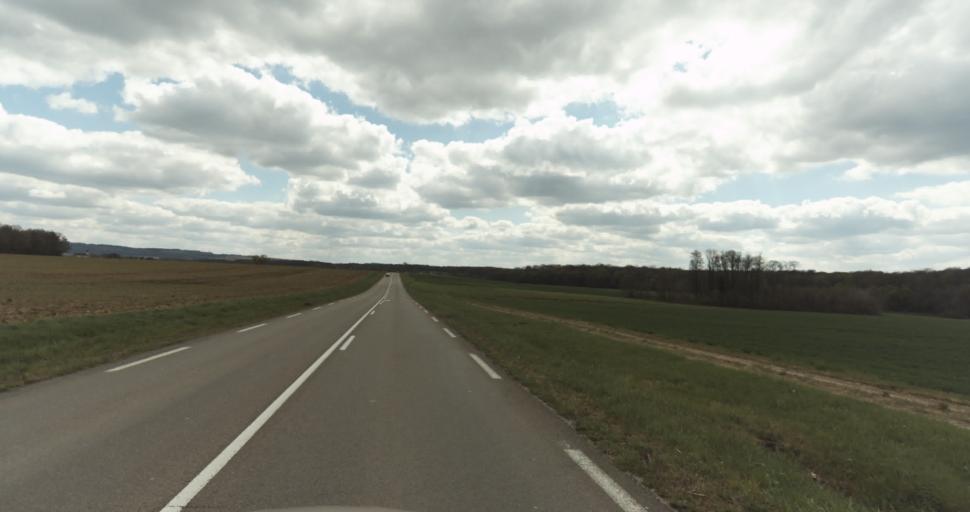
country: FR
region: Bourgogne
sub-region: Departement de la Cote-d'Or
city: Auxonne
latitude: 47.1529
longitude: 5.4158
